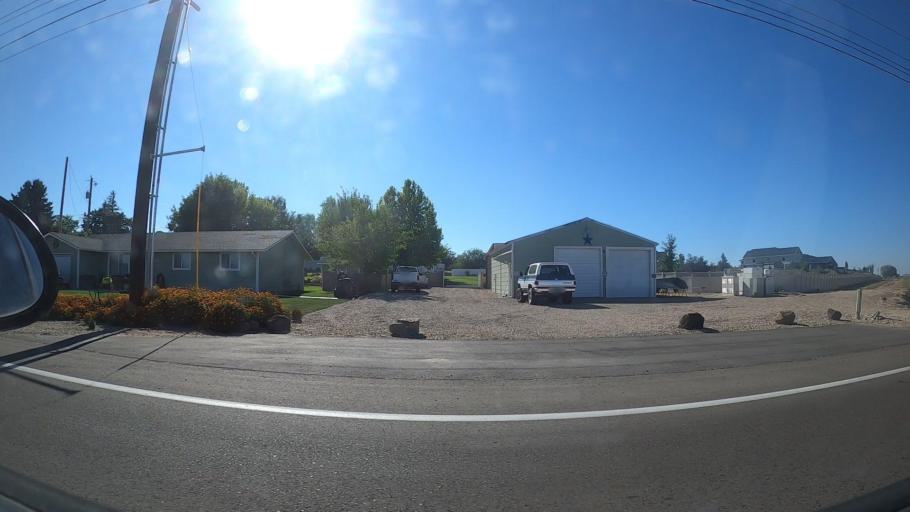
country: US
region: Idaho
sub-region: Canyon County
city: Nampa
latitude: 43.5602
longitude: -116.6129
